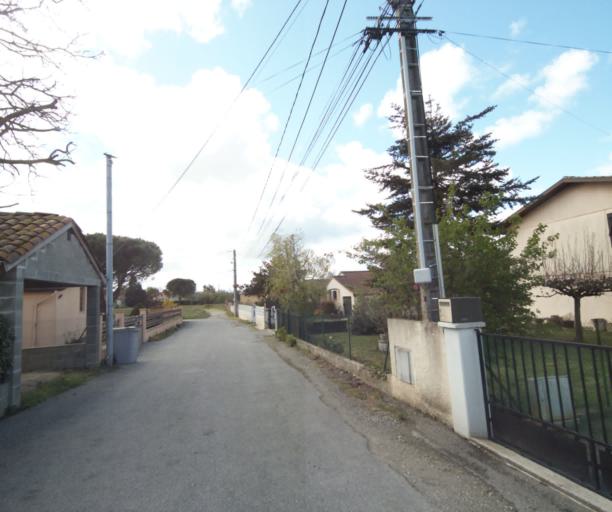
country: FR
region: Midi-Pyrenees
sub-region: Departement de l'Ariege
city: Saverdun
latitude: 43.2281
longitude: 1.5764
